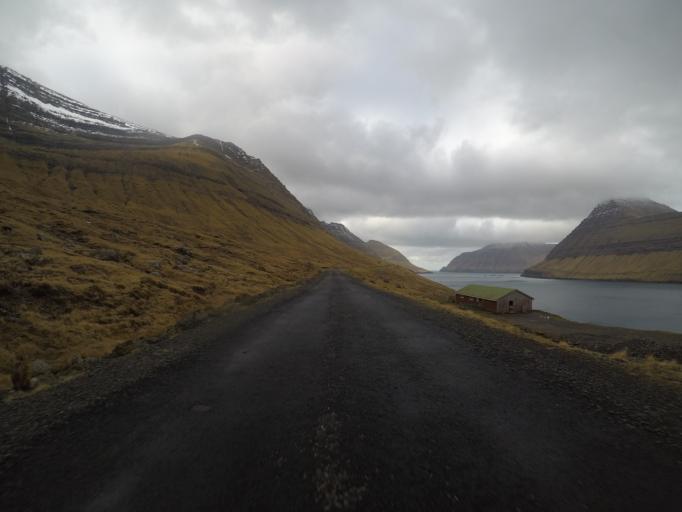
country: FO
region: Nordoyar
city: Klaksvik
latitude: 62.3168
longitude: -6.5557
